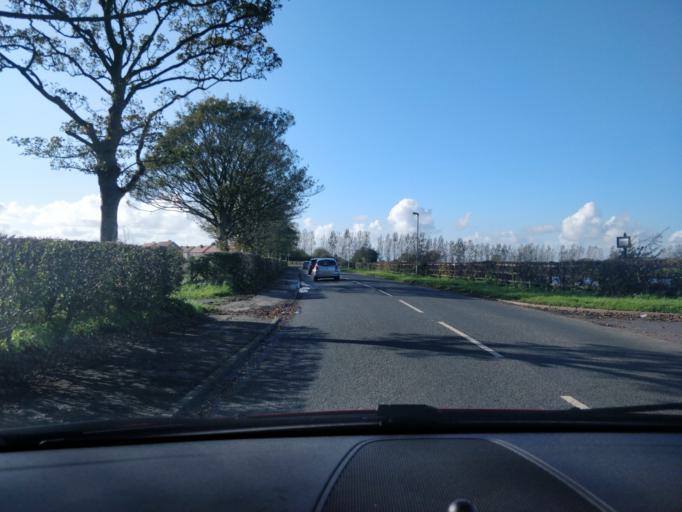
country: GB
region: England
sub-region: Lancashire
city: Banks
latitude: 53.6808
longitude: -2.9378
